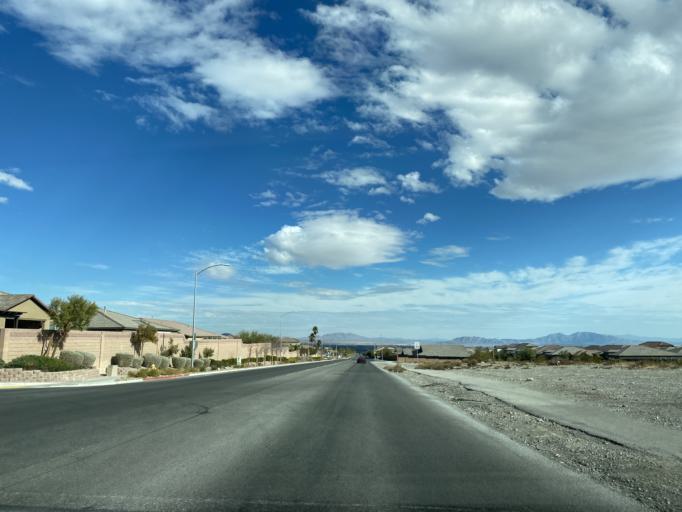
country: US
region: Nevada
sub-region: Clark County
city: Summerlin South
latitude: 36.2847
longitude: -115.3099
